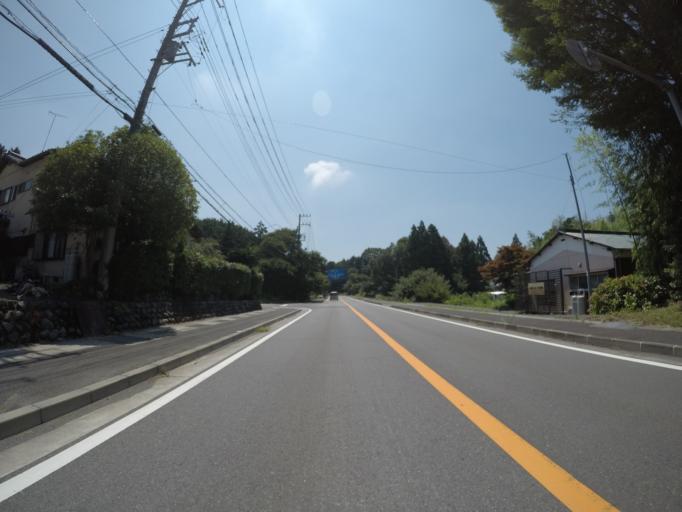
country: JP
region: Shizuoka
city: Fujinomiya
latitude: 35.2673
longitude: 138.6311
